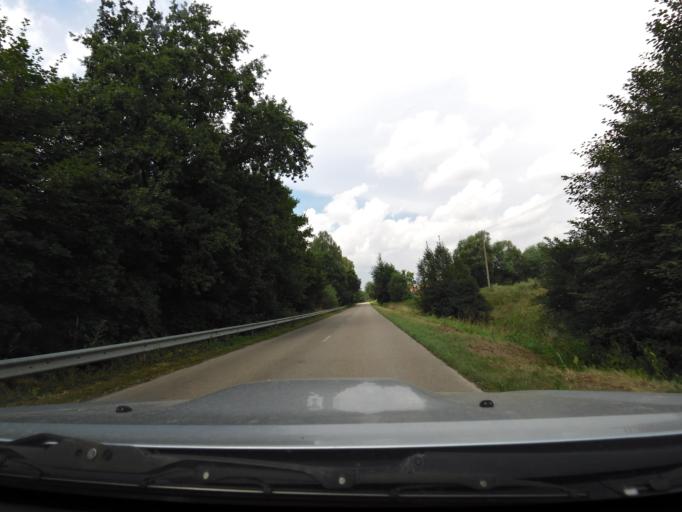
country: RU
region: Kaliningrad
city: Neman
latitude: 55.0959
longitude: 22.0208
